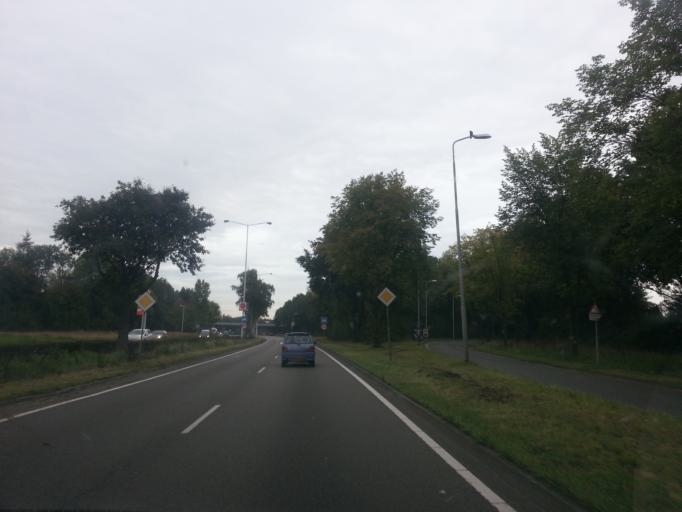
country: NL
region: North Brabant
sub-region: Gemeente Son en Breugel
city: Son
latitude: 51.4821
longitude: 5.4897
